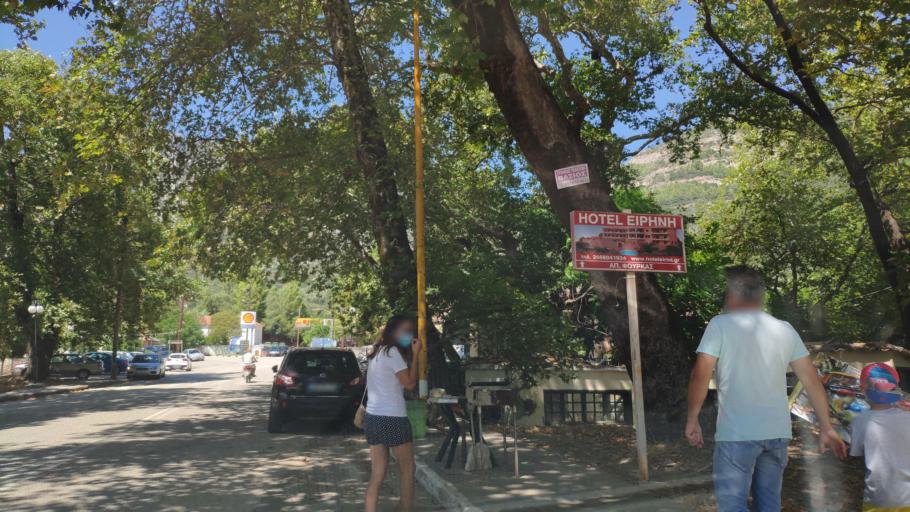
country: GR
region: Epirus
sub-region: Nomos Prevezis
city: Kanalaki
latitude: 39.3259
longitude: 20.6074
